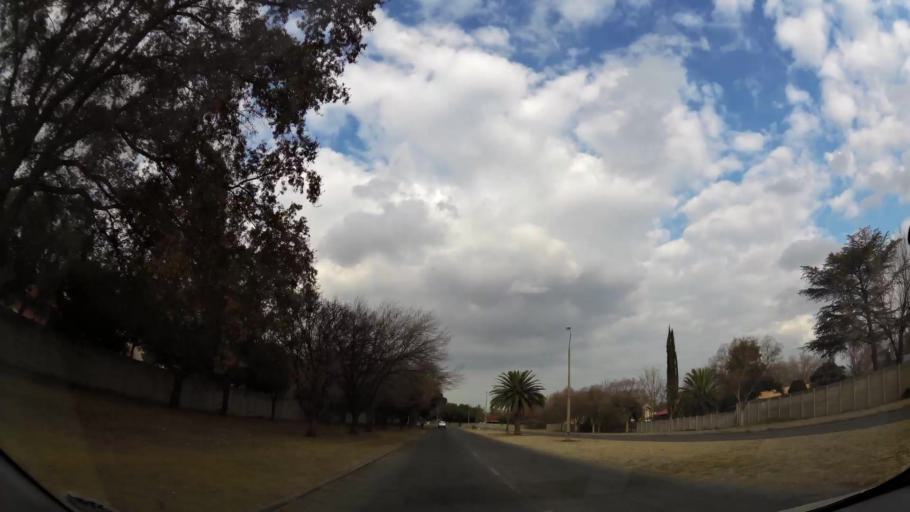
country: ZA
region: Orange Free State
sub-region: Fezile Dabi District Municipality
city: Sasolburg
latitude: -26.8194
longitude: 27.8230
